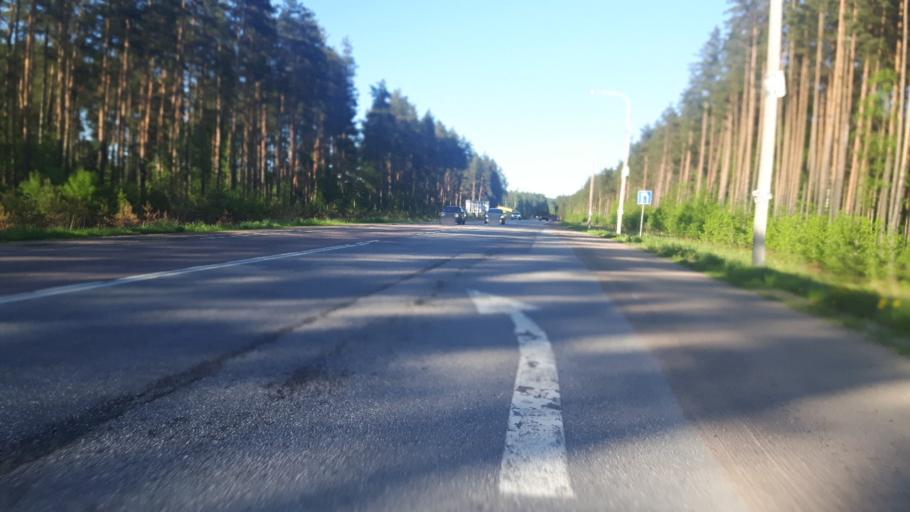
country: RU
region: Leningrad
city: Molodezhnoye
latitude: 60.1712
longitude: 29.4312
